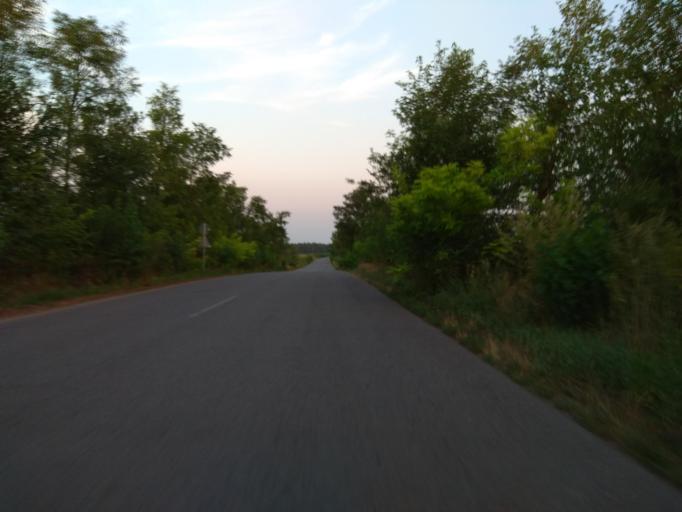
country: HU
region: Borsod-Abauj-Zemplen
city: Emod
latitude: 47.9147
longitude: 20.8481
